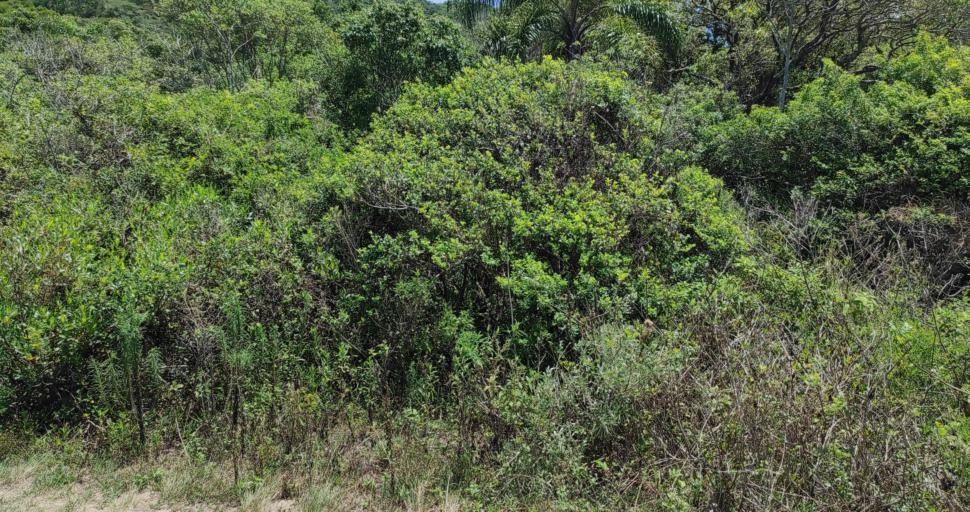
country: BR
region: Santa Catarina
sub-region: Porto Belo
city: Porto Belo
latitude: -27.1966
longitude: -48.5598
